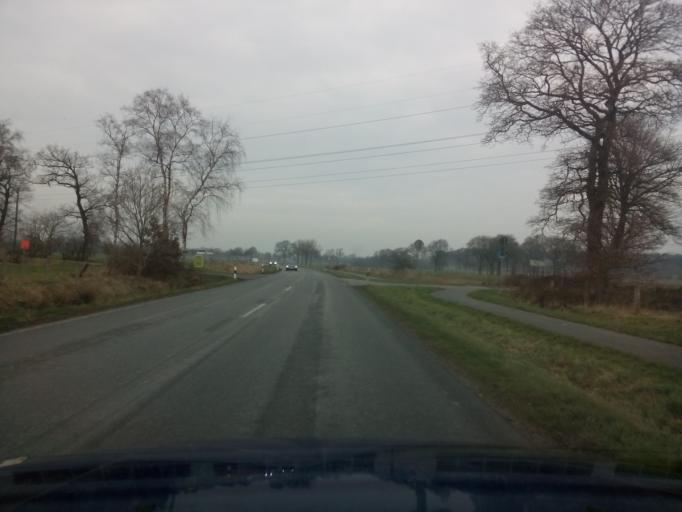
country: DE
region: Lower Saxony
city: Kuhrstedt
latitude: 53.6134
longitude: 8.8228
